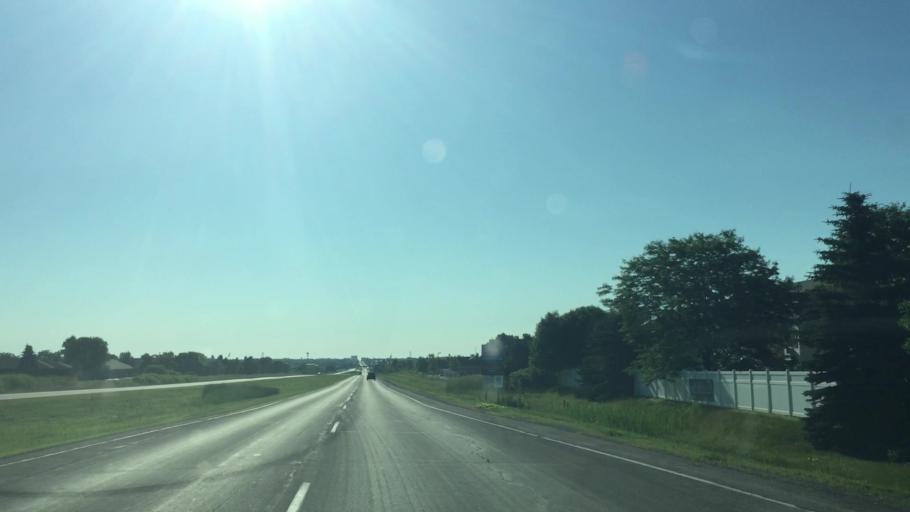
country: US
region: Wisconsin
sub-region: Winnebago County
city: Menasha
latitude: 44.2620
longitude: -88.4960
